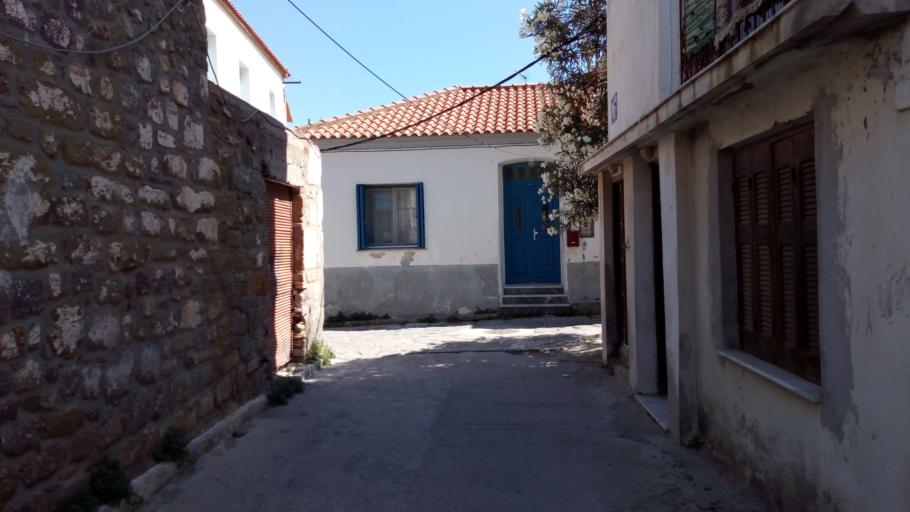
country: GR
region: North Aegean
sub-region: Nomos Lesvou
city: Myrina
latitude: 39.8755
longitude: 25.0604
